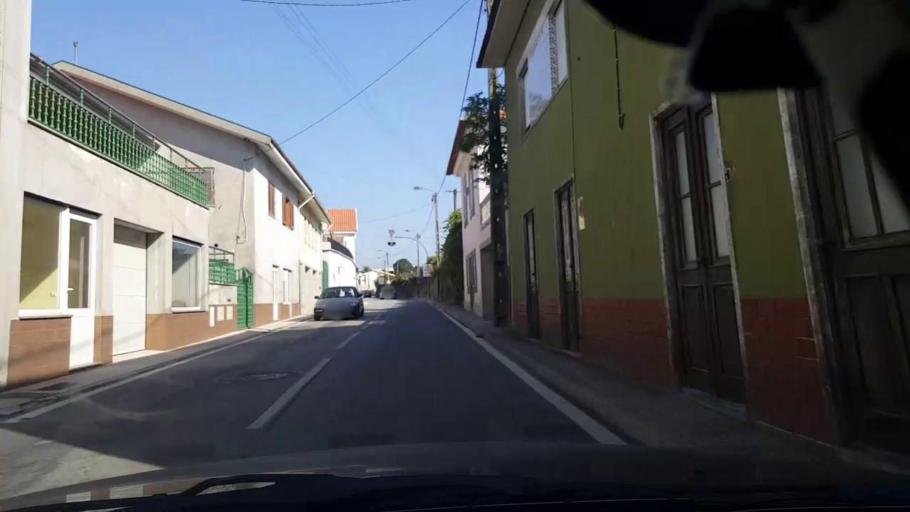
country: PT
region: Porto
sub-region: Maia
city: Gemunde
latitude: 41.3046
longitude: -8.6787
